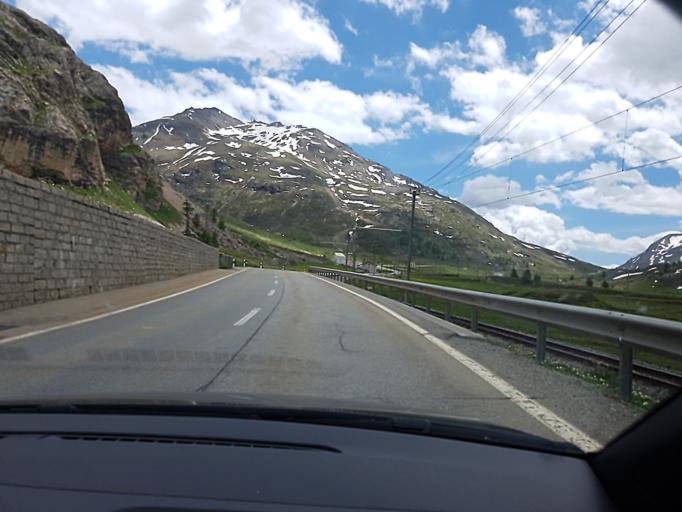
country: CH
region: Grisons
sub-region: Maloja District
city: Pontresina
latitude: 46.4405
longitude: 9.9867
